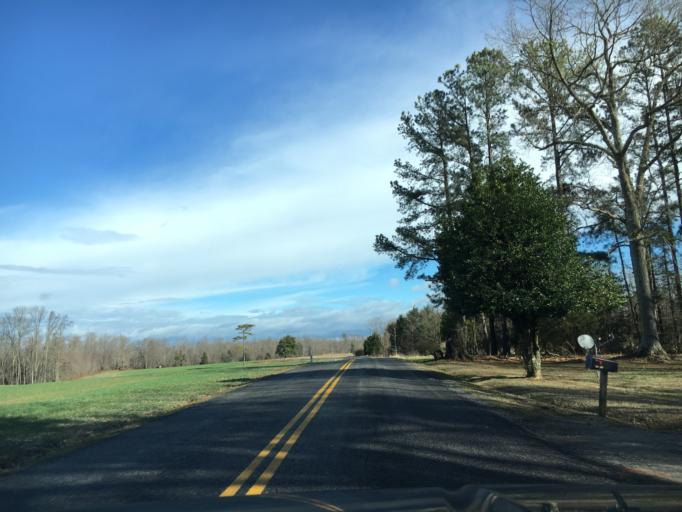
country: US
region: Virginia
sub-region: Amelia County
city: Amelia Court House
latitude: 37.4215
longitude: -78.0700
